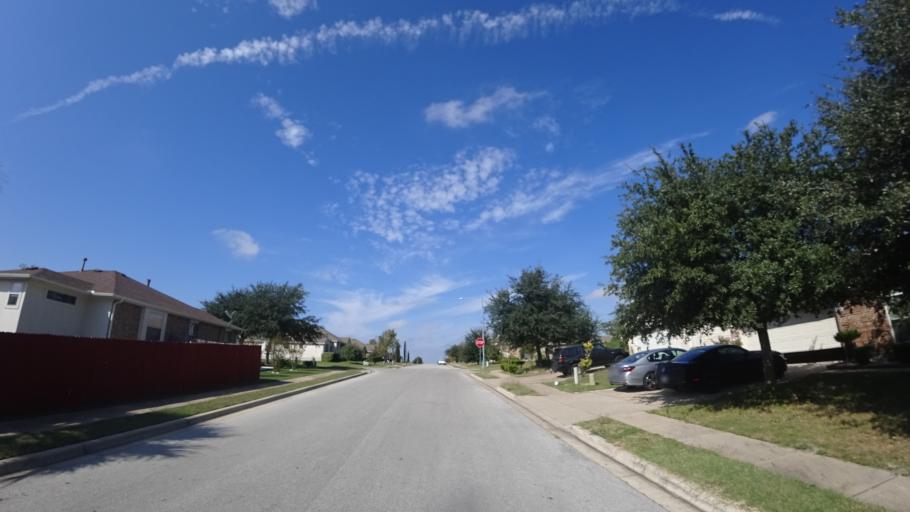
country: US
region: Texas
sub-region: Travis County
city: Pflugerville
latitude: 30.4196
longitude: -97.6320
